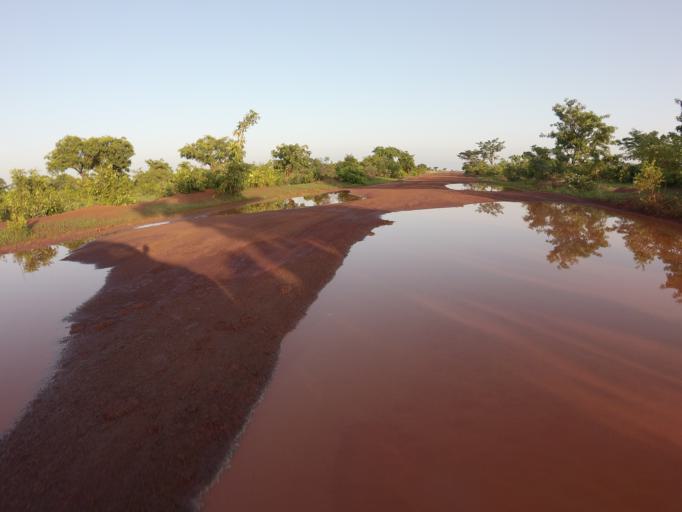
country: TG
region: Savanes
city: Sansanne-Mango
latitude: 10.2346
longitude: -0.0738
